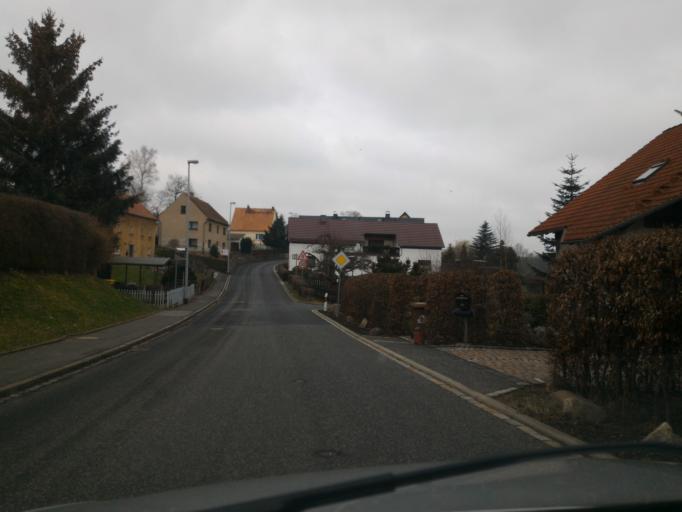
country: DE
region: Saxony
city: Olbersdorf
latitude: 50.8603
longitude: 14.7913
